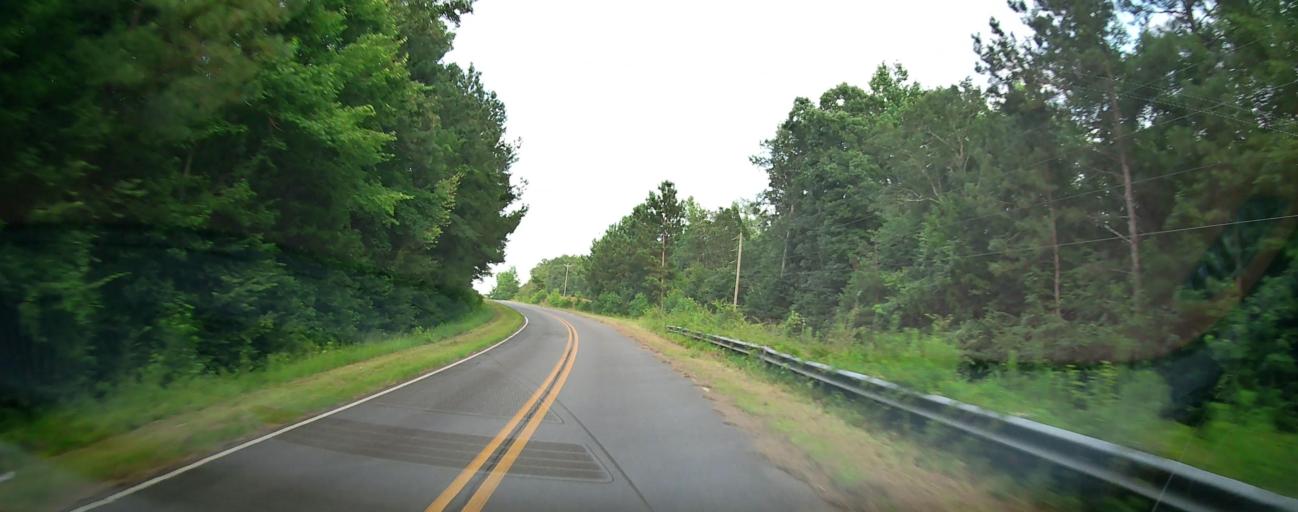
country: US
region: Georgia
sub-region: Crawford County
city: Roberta
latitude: 32.6717
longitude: -84.0792
